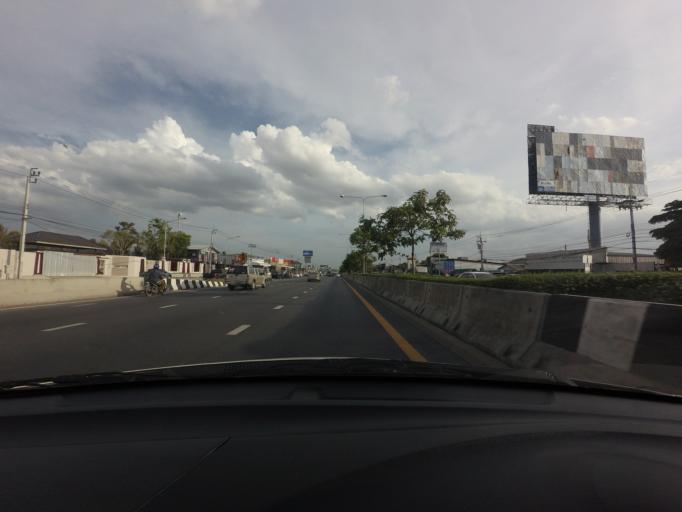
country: TH
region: Nonthaburi
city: Bang Bua Thong
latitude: 13.9216
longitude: 100.4523
